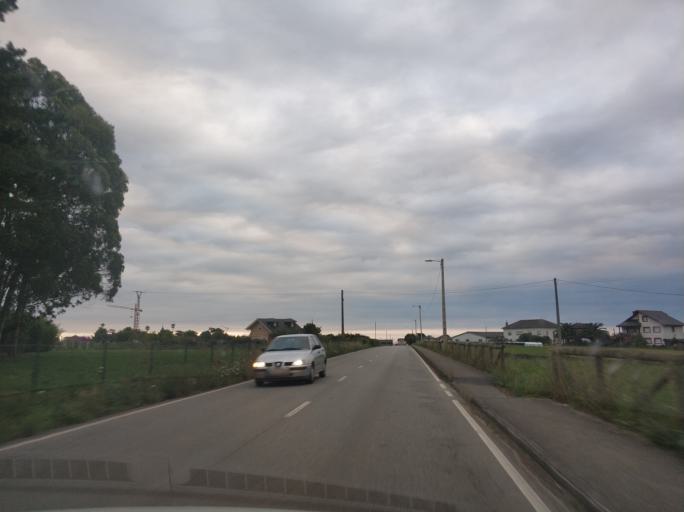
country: ES
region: Asturias
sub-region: Province of Asturias
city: Navia
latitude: 43.5372
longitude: -6.5204
